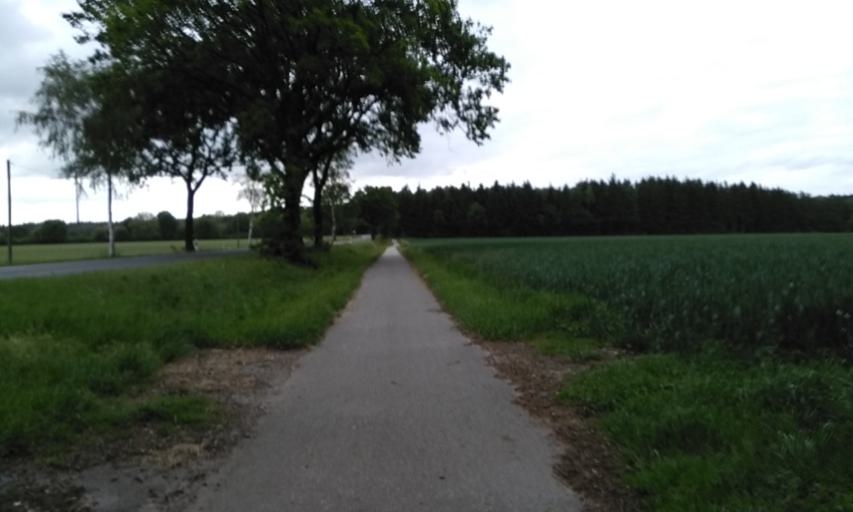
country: DE
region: Lower Saxony
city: Harsefeld
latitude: 53.4898
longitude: 9.4927
